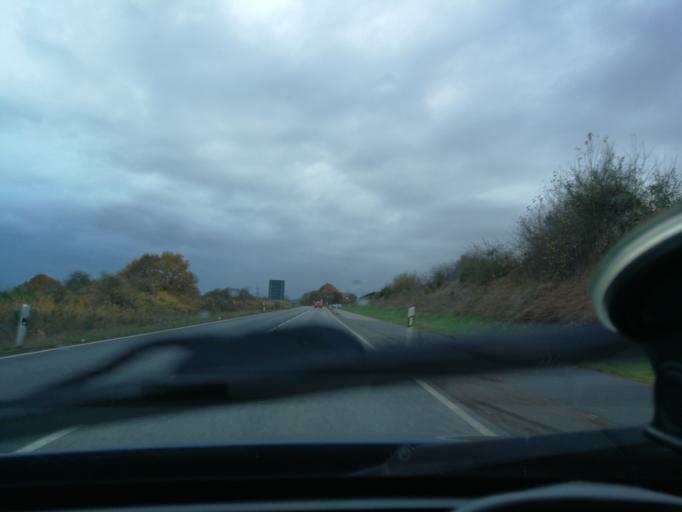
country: DE
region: Rheinland-Pfalz
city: Altrich
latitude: 49.9759
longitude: 6.9238
